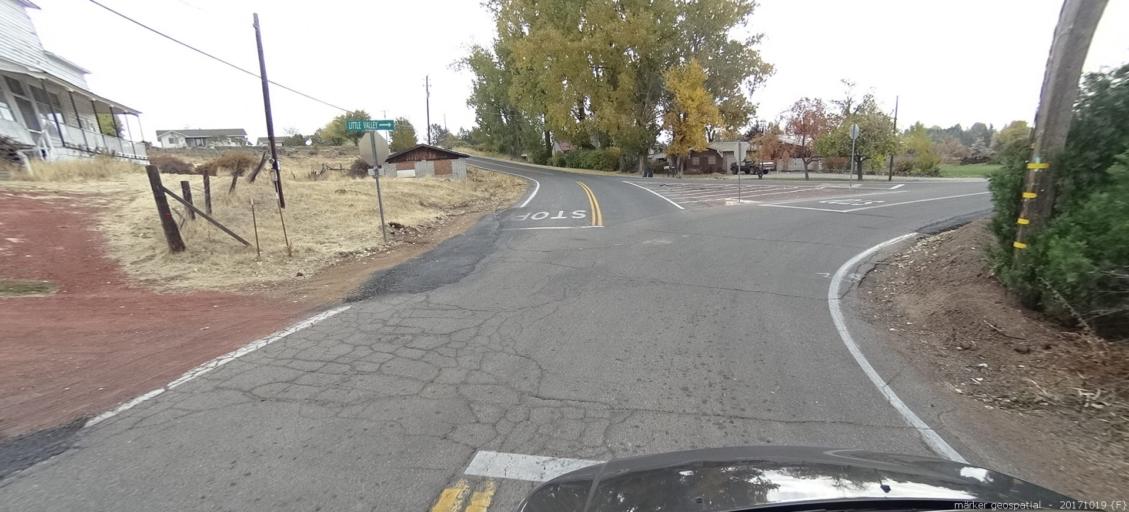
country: US
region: California
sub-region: Shasta County
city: Burney
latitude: 41.0477
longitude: -121.3316
